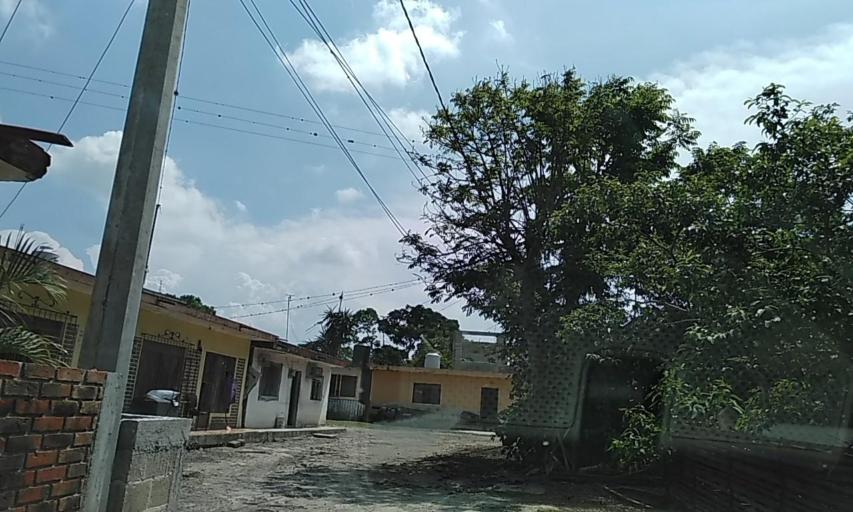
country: MX
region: Veracruz
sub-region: Emiliano Zapata
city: Dos Rios
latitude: 19.4438
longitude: -96.7818
